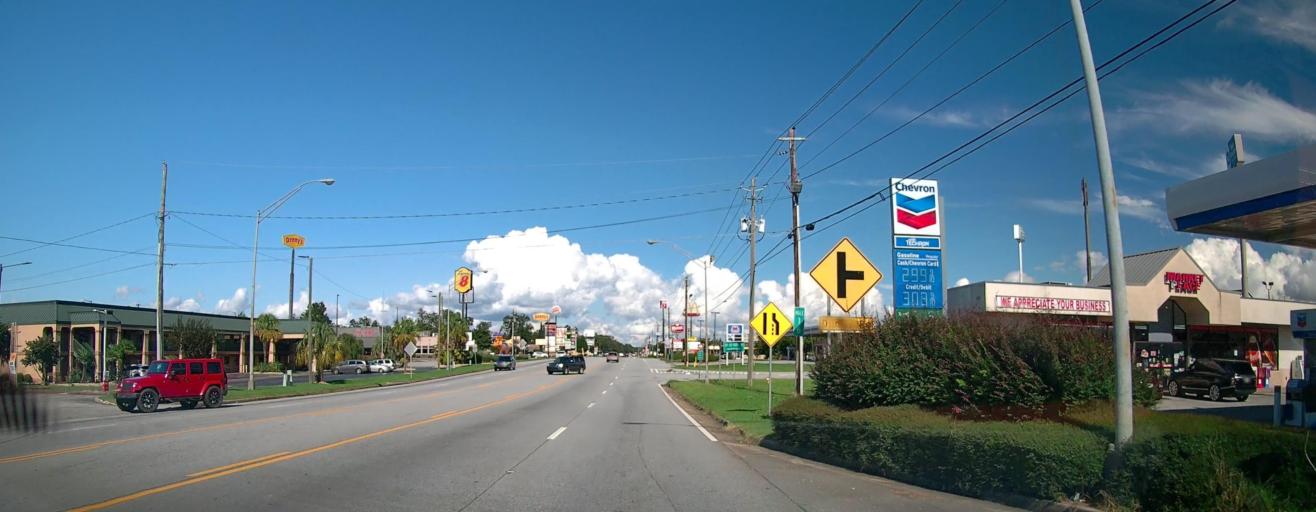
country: US
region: Georgia
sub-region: Peach County
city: Byron
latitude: 32.6614
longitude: -83.7426
